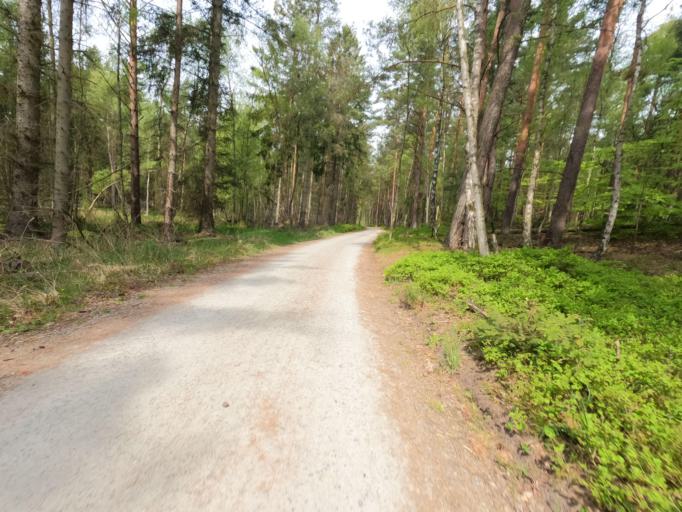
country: DE
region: Mecklenburg-Vorpommern
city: Ostseebad Prerow
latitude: 54.4536
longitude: 12.5149
